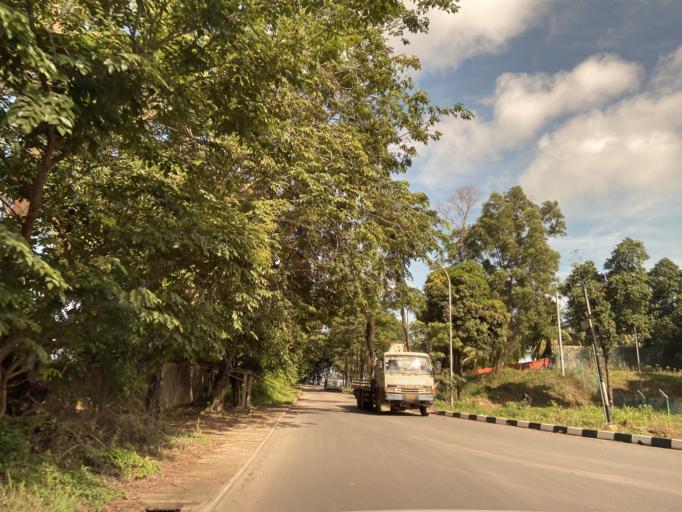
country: SG
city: Singapore
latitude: 1.1742
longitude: 104.0113
